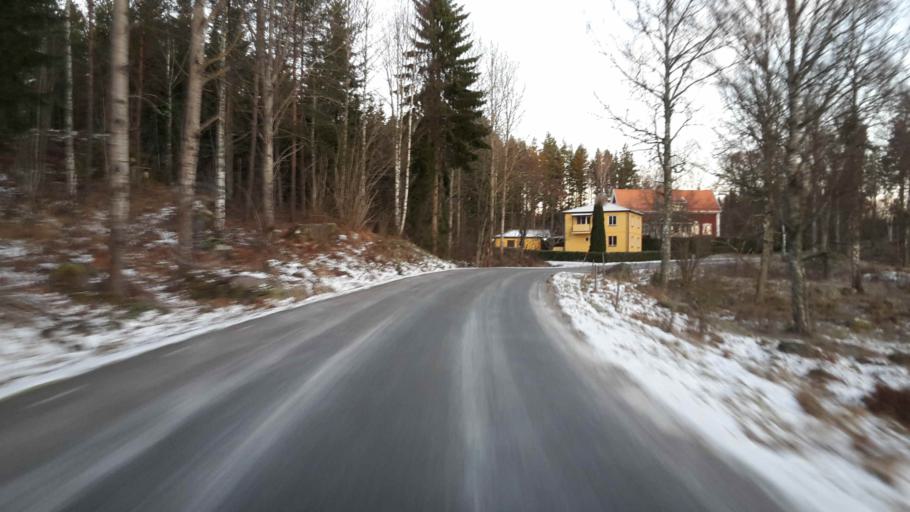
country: SE
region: OEstergoetland
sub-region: Atvidabergs Kommun
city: Atvidaberg
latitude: 58.2579
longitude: 16.1012
